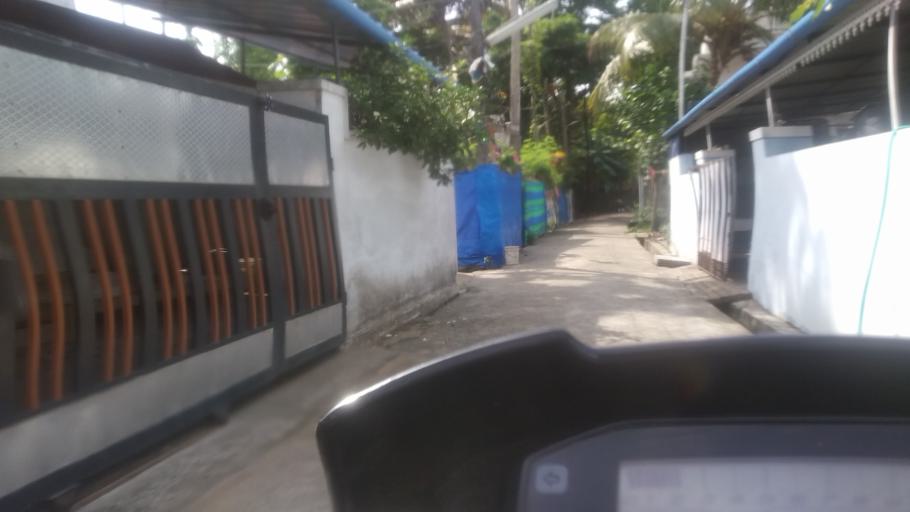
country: IN
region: Kerala
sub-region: Ernakulam
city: Elur
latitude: 10.0712
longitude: 76.2100
